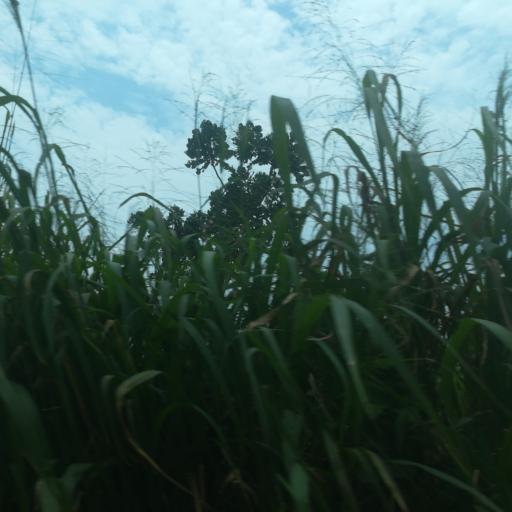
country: NG
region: Lagos
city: Ejirin
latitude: 6.6485
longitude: 3.7376
